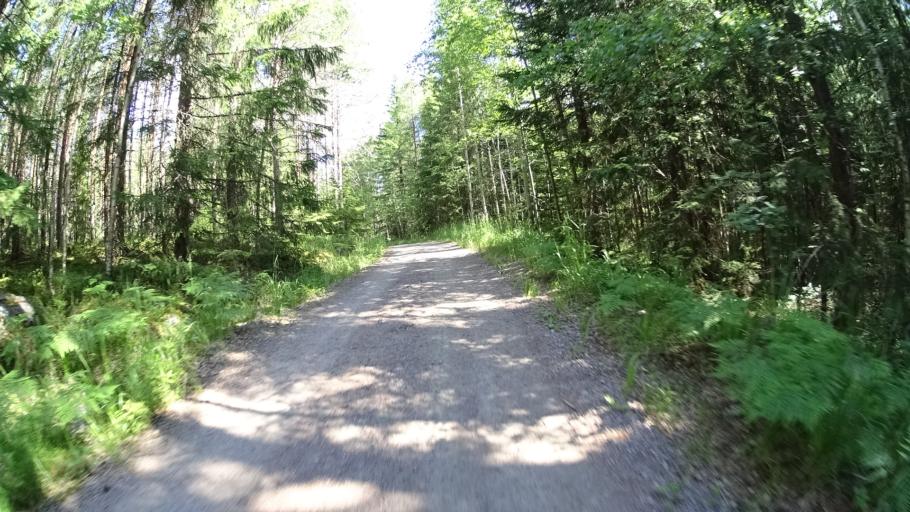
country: FI
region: Uusimaa
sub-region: Helsinki
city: Vihti
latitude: 60.3235
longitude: 24.4564
